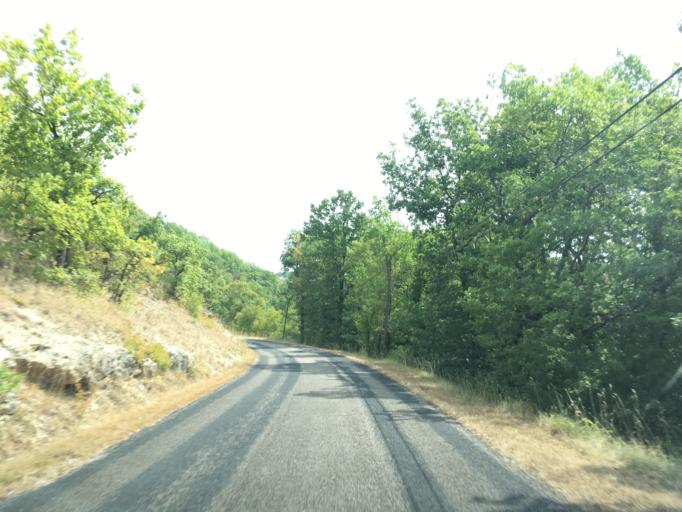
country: FR
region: Midi-Pyrenees
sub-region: Departement du Lot
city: Le Vigan
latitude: 44.7427
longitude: 1.5146
